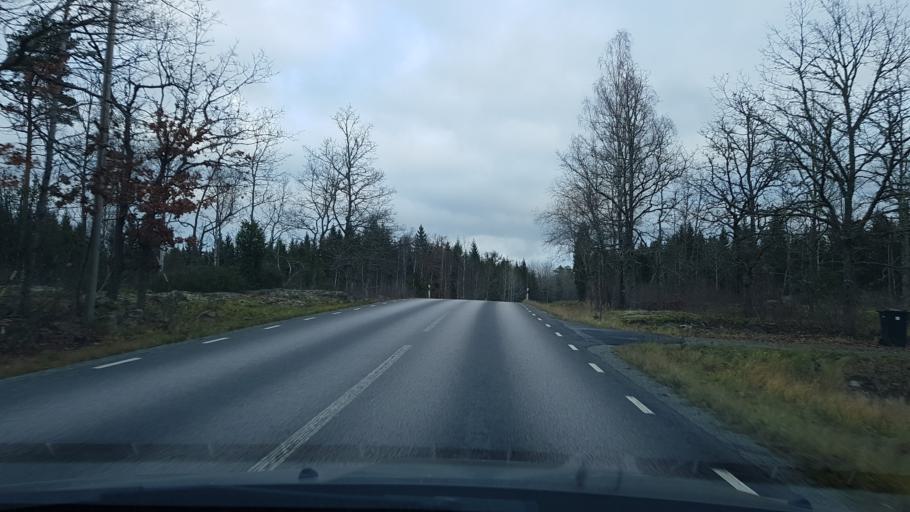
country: SE
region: Stockholm
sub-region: Norrtalje Kommun
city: Skanninge
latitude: 60.0325
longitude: 18.4428
